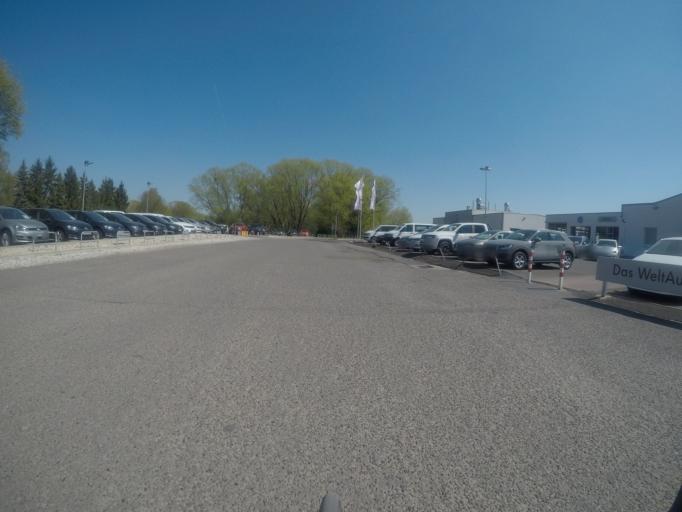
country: DE
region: Brandenburg
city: Bernau bei Berlin
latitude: 52.6712
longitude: 13.5843
